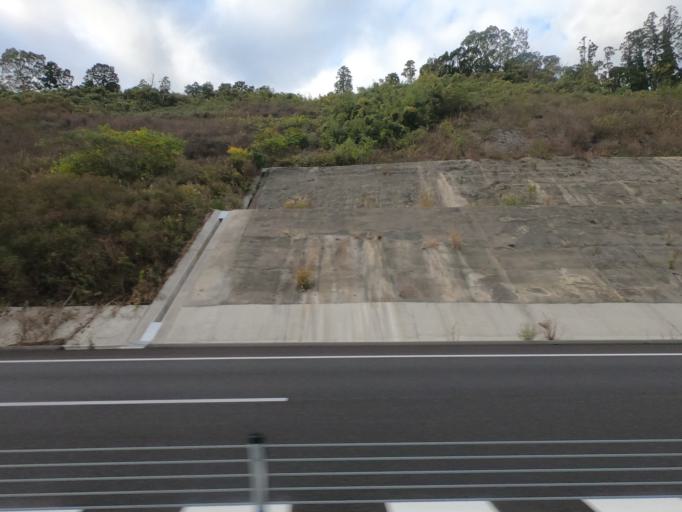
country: JP
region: Kumamoto
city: Minamata
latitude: 32.2391
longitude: 130.4610
